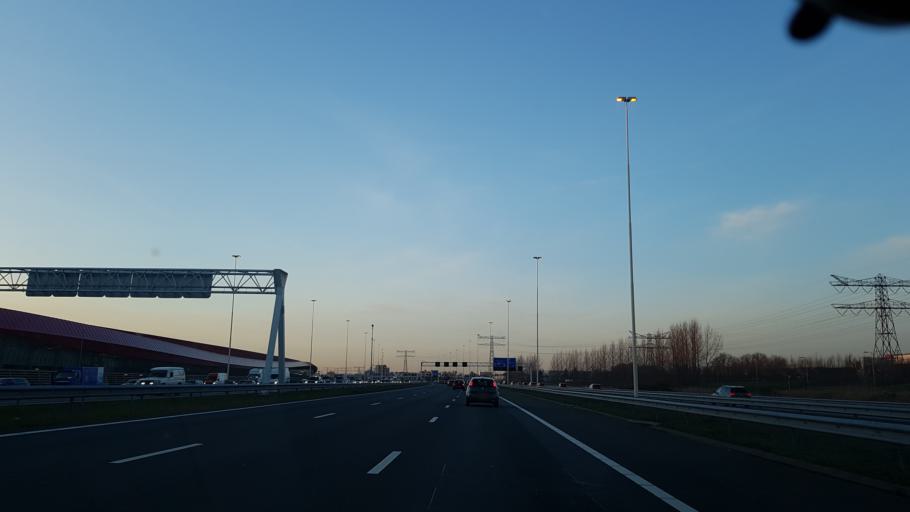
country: NL
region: Utrecht
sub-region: Stichtse Vecht
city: Maarssen
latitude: 52.1037
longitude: 5.0627
